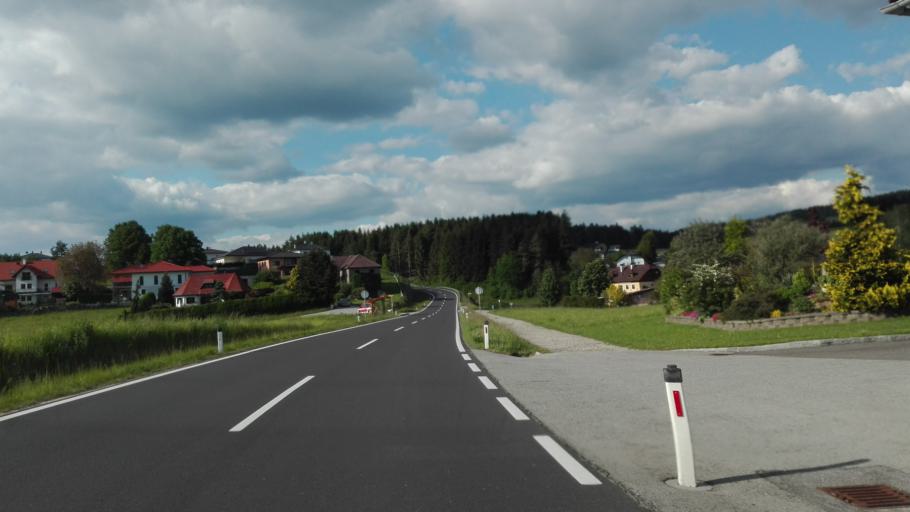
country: AT
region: Upper Austria
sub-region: Politischer Bezirk Perg
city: Perg
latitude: 48.3584
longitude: 14.6803
